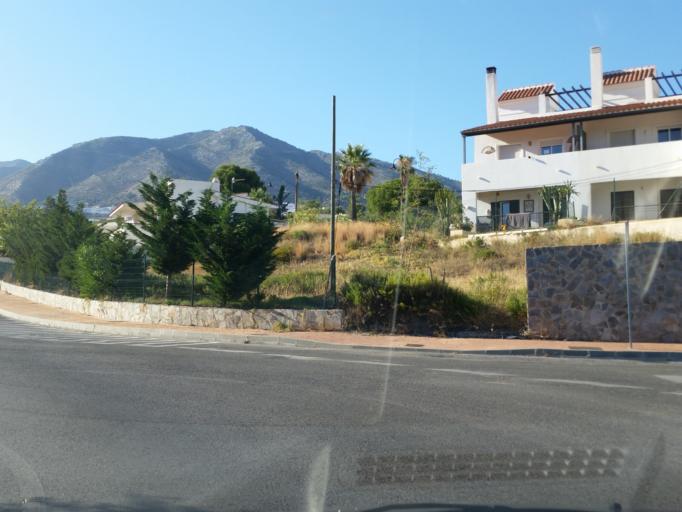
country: ES
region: Andalusia
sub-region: Provincia de Malaga
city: Mijas
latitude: 36.5745
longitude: -4.6357
